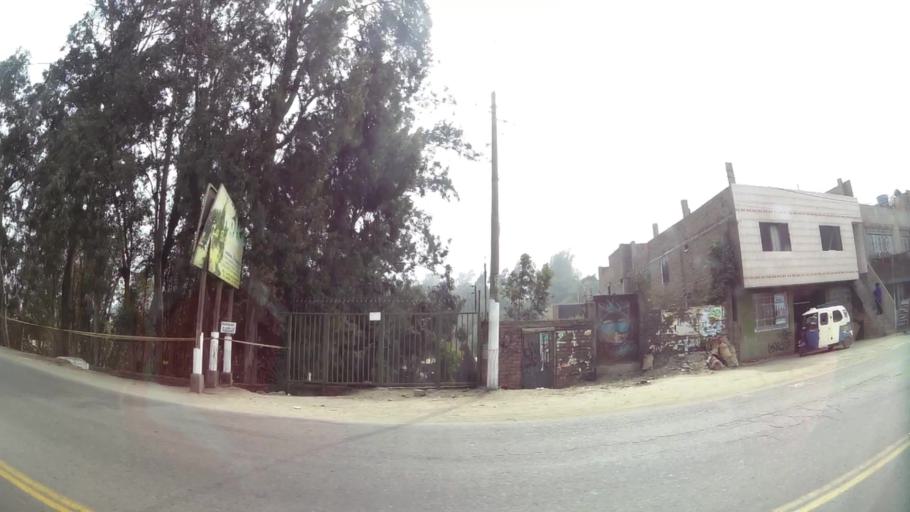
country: PE
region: Lima
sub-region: Lima
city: Chaclacayo
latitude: -11.9665
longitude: -76.7446
